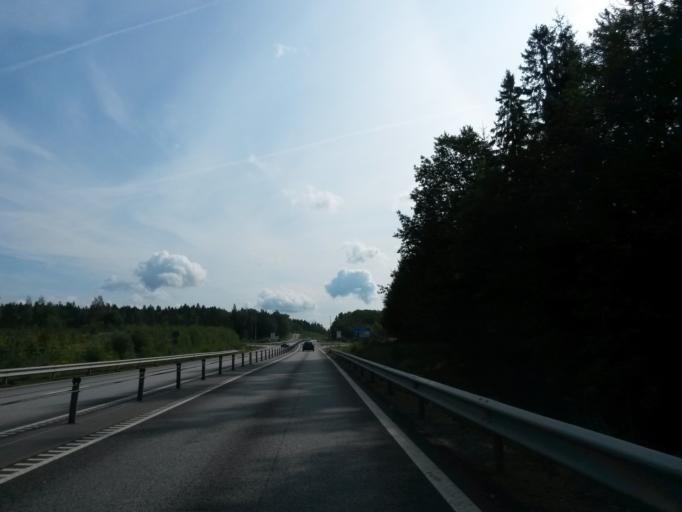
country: SE
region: Kronoberg
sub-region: Alvesta Kommun
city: Alvesta
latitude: 56.9207
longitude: 14.5918
